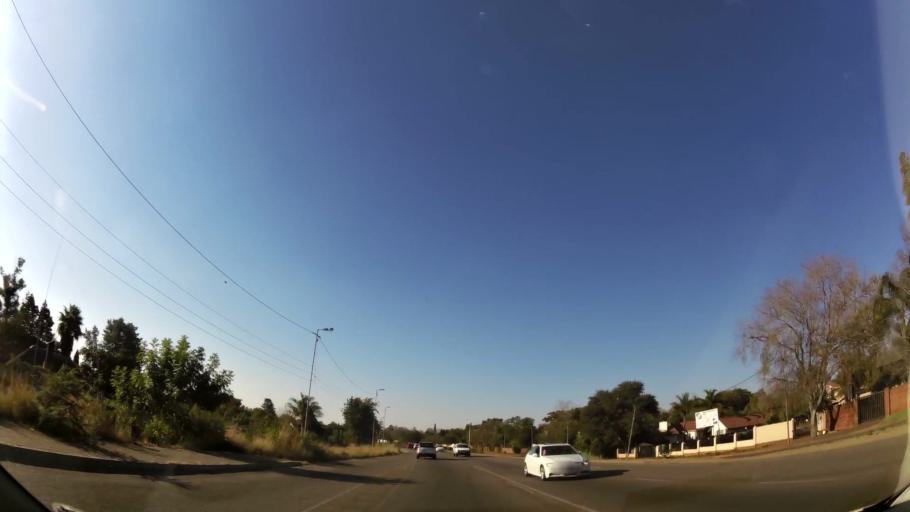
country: ZA
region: Gauteng
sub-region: City of Tshwane Metropolitan Municipality
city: Centurion
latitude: -25.8496
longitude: 28.1503
